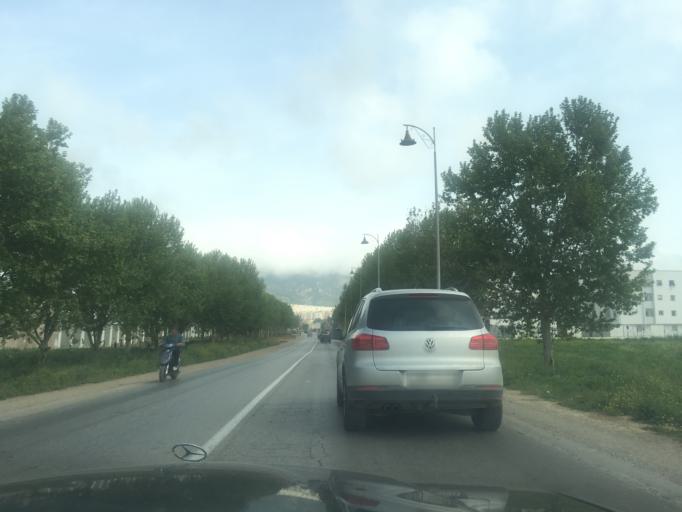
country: MA
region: Fes-Boulemane
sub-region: Fes
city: Fes
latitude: 34.0368
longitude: -5.0327
